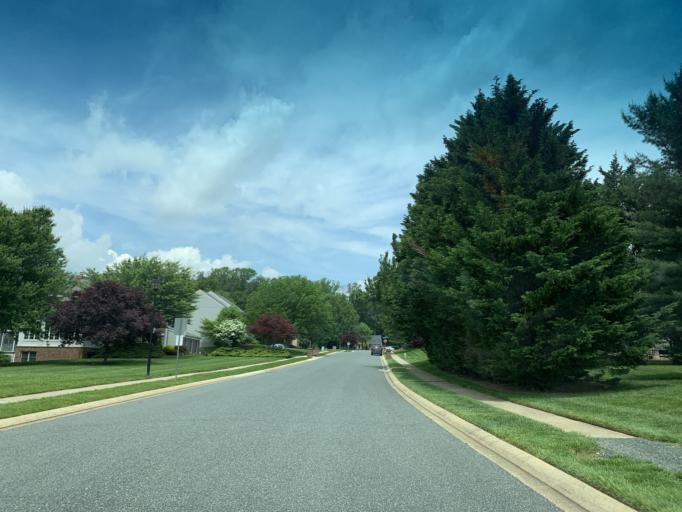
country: US
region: Maryland
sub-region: Harford County
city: South Bel Air
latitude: 39.5565
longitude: -76.3372
